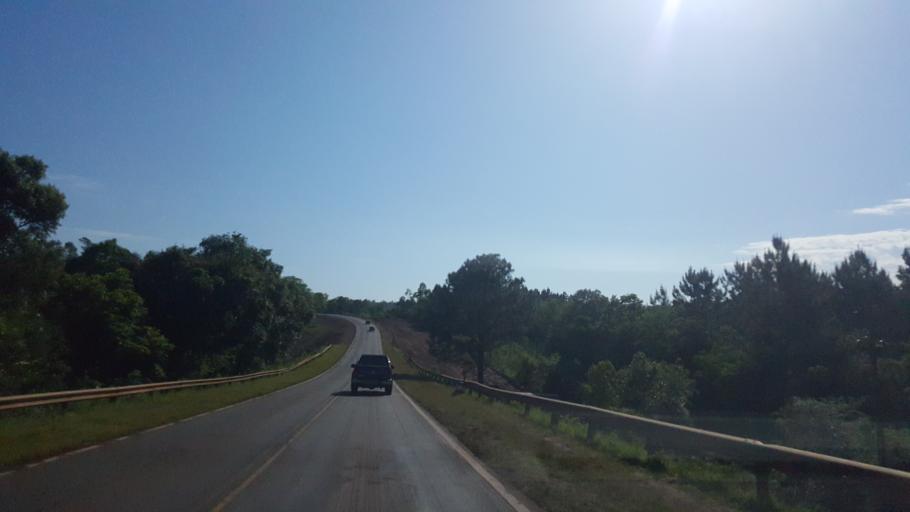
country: AR
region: Misiones
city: Santa Ana
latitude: -27.3693
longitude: -55.5631
